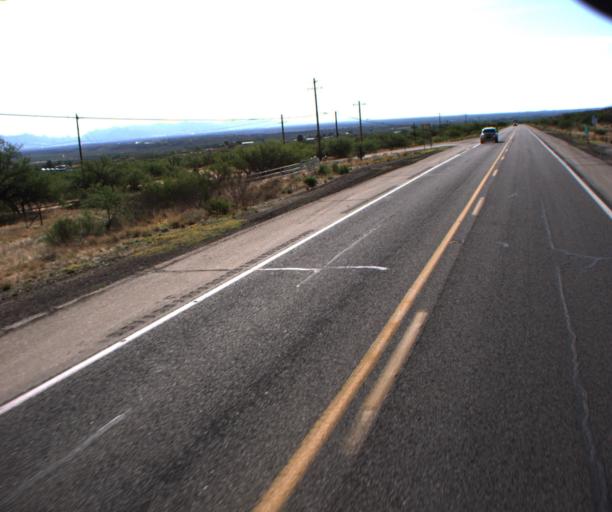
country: US
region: Arizona
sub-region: Cochise County
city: Benson
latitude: 31.9311
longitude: -110.2823
